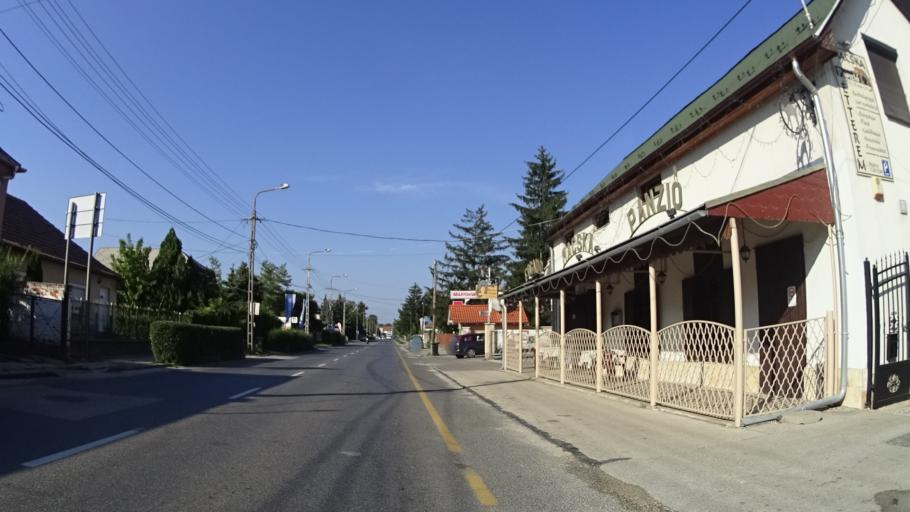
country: HU
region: Fejer
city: Martonvasar
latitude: 47.3157
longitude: 18.7903
